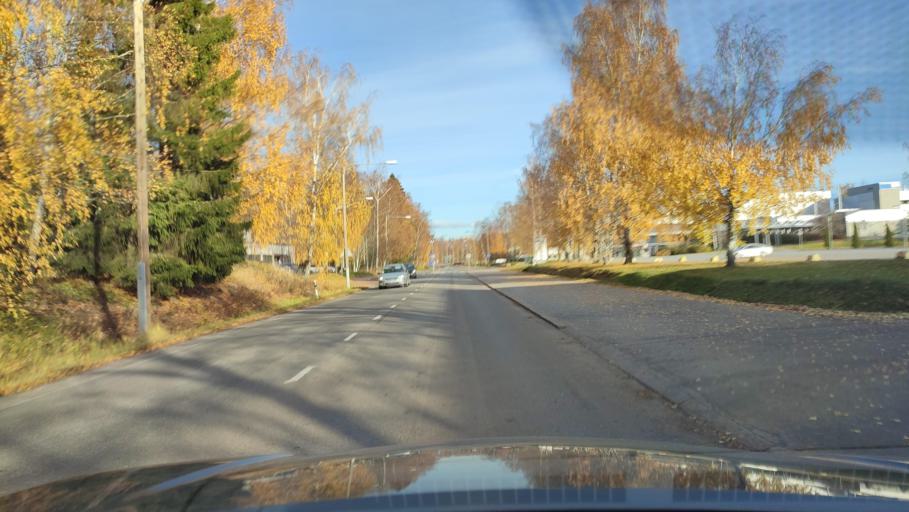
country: FI
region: Ostrobothnia
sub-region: Vaasa
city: Vaasa
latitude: 63.0854
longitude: 21.6424
